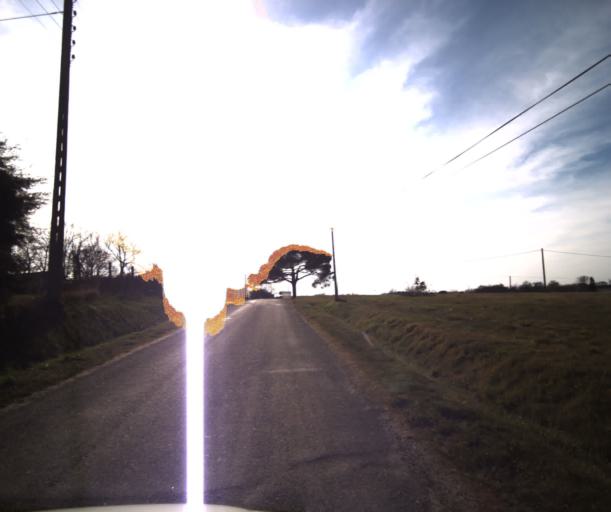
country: FR
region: Midi-Pyrenees
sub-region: Departement du Tarn-et-Garonne
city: Corbarieu
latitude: 43.9350
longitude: 1.3428
